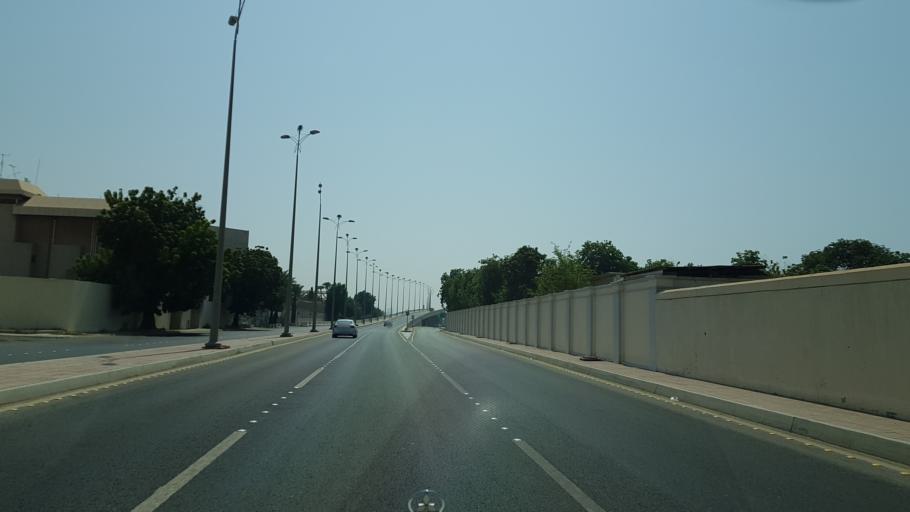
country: SA
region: Makkah
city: Jeddah
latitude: 21.5451
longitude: 39.1539
